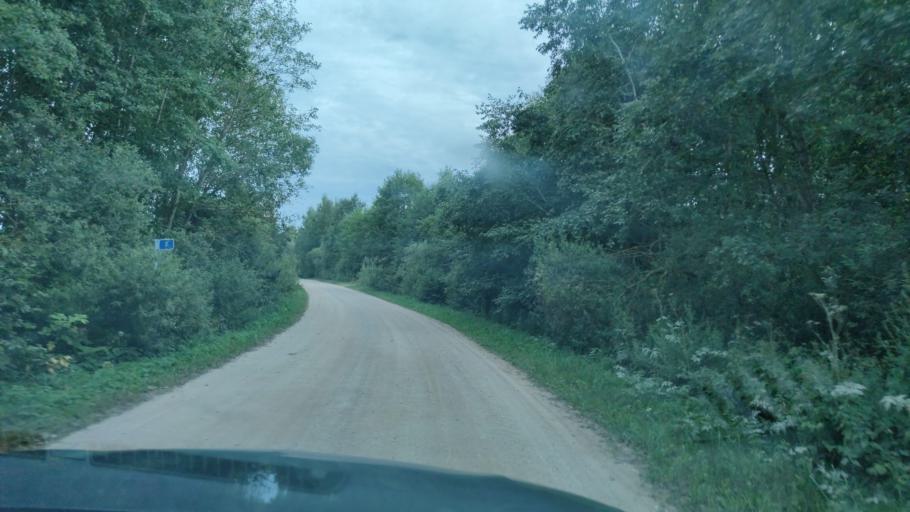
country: BY
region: Vitebsk
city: Pastavy
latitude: 55.1147
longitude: 27.1466
